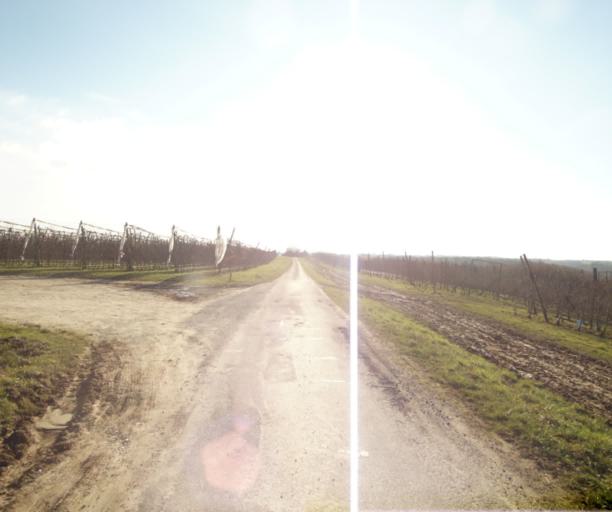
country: FR
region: Midi-Pyrenees
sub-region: Departement du Tarn-et-Garonne
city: Moissac
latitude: 44.1349
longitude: 1.0549
